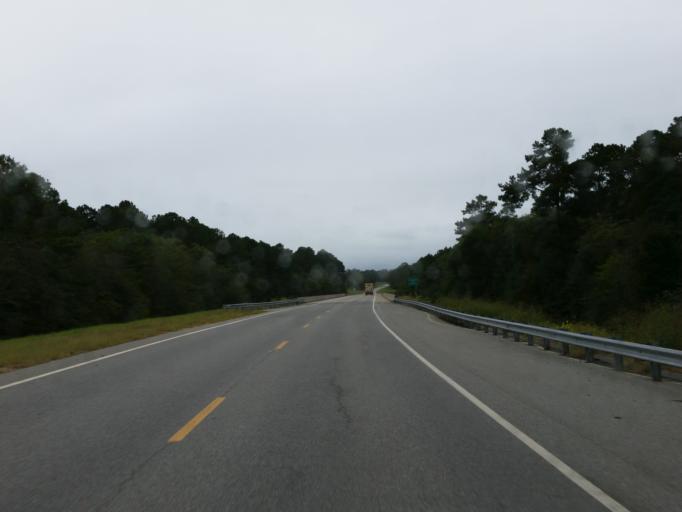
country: US
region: Georgia
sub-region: Cook County
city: Adel
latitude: 31.1218
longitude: -83.3248
